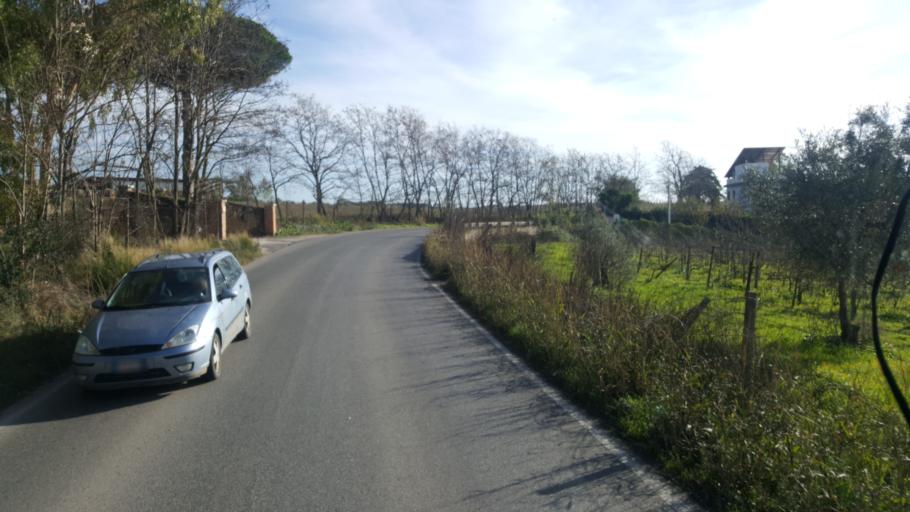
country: IT
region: Latium
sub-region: Citta metropolitana di Roma Capitale
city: Mantiglia di Ardea
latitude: 41.6902
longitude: 12.5996
